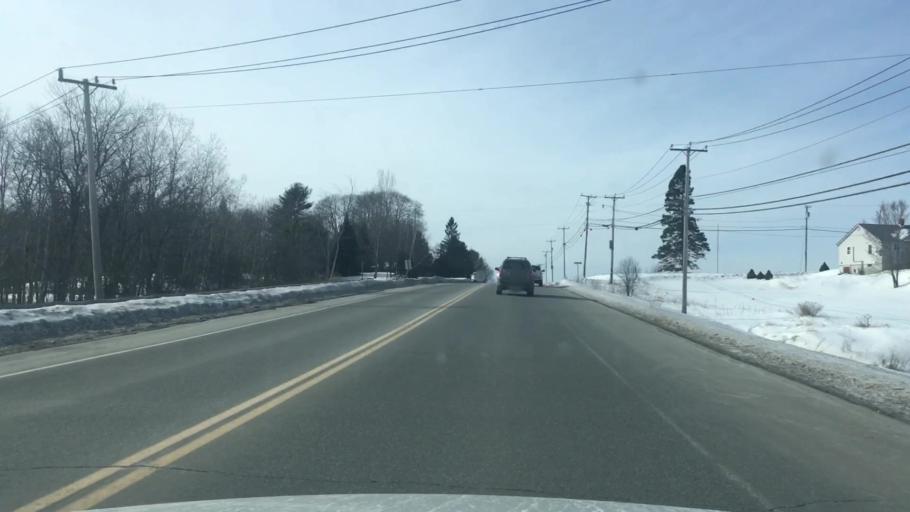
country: US
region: Maine
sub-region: Penobscot County
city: Bangor
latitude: 44.8526
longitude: -68.8092
